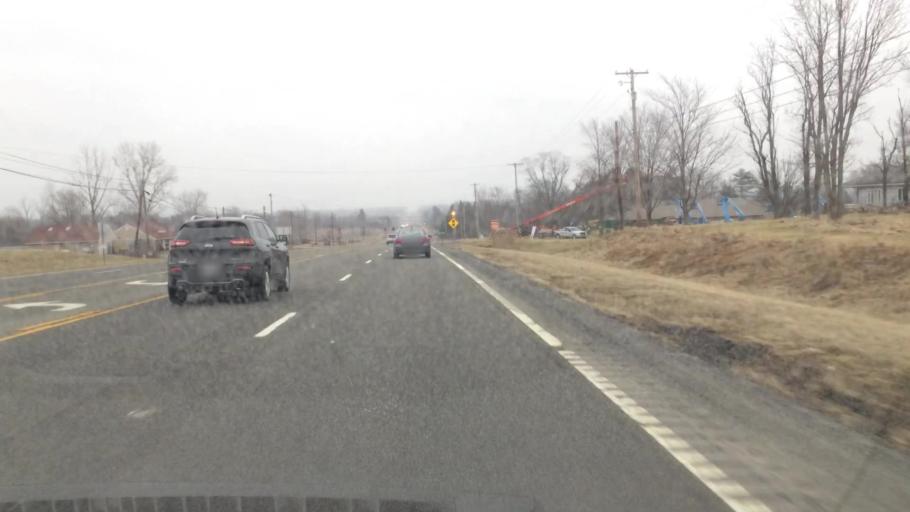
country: US
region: Ohio
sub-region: Medina County
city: Medina
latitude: 41.1362
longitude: -81.7603
